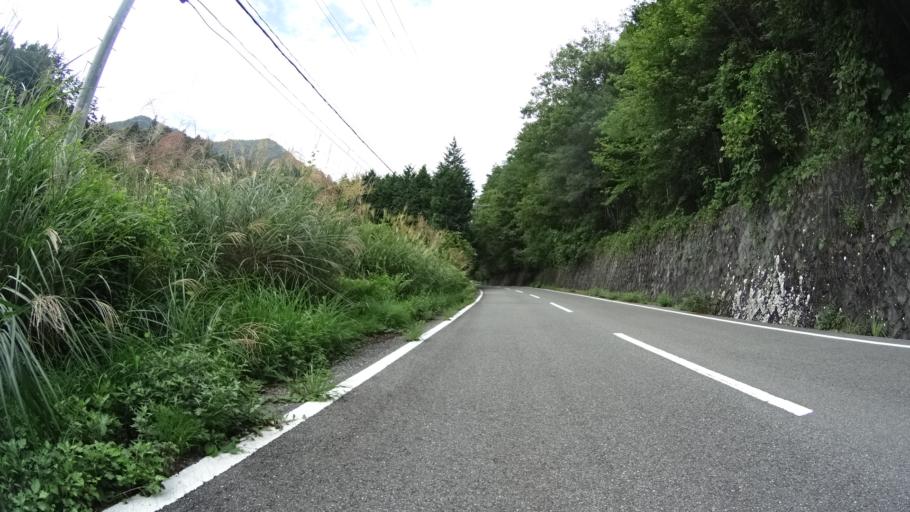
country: JP
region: Yamanashi
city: Kofu-shi
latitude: 35.7669
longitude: 138.5498
